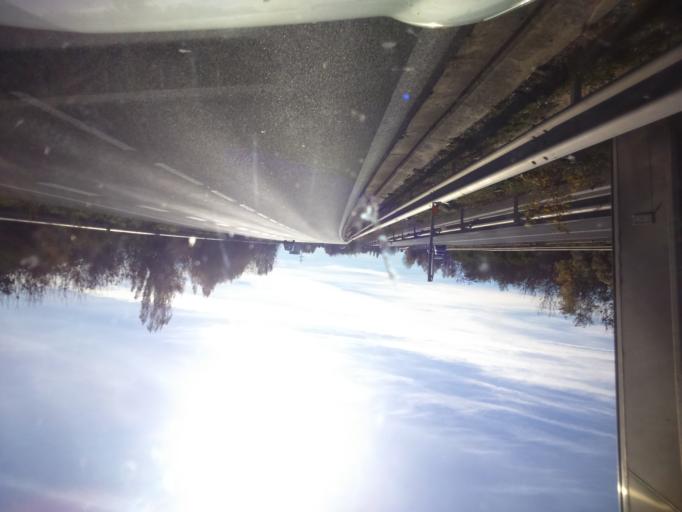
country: FR
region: Poitou-Charentes
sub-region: Departement de la Charente-Maritime
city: Breuil-Magne
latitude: 45.9703
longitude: -0.9843
